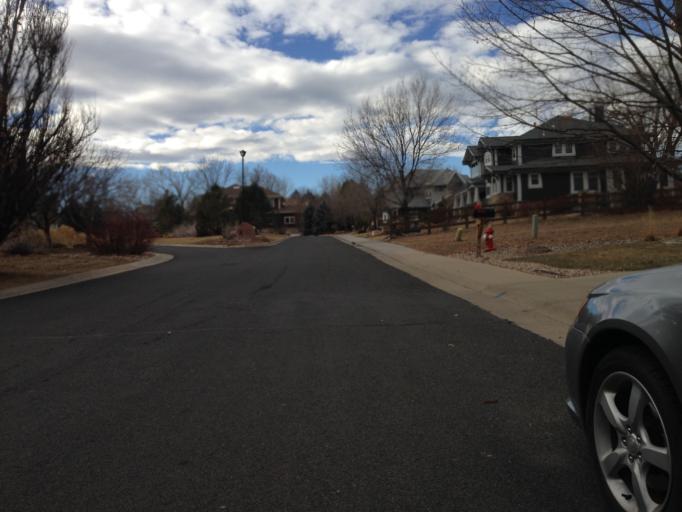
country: US
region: Colorado
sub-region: Boulder County
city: Louisville
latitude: 39.9792
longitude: -105.1448
